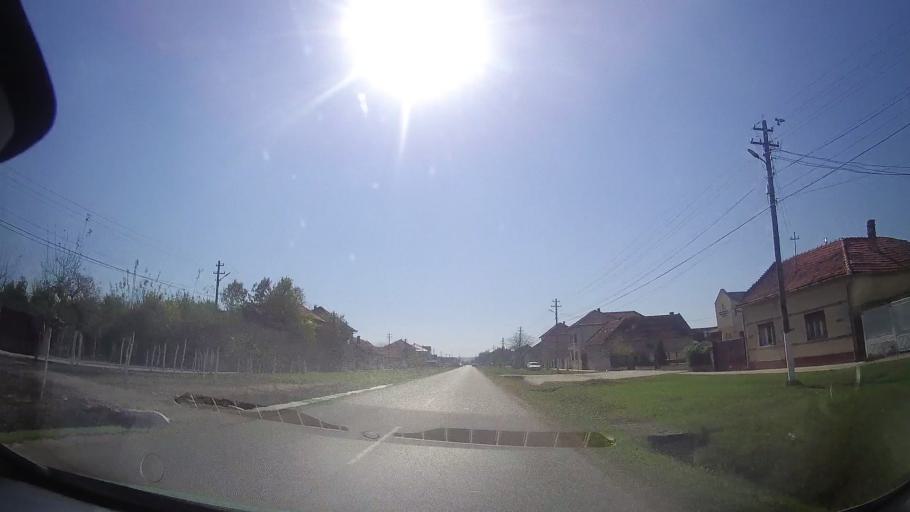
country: RO
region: Timis
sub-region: Comuna Bethausen
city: Bethausen
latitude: 45.8344
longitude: 21.9596
